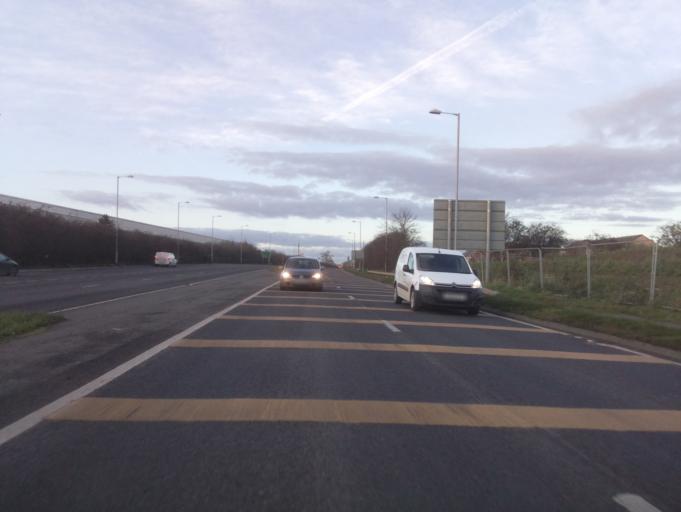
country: GB
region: England
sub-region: Staffordshire
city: Stafford
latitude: 52.8336
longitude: -2.1328
